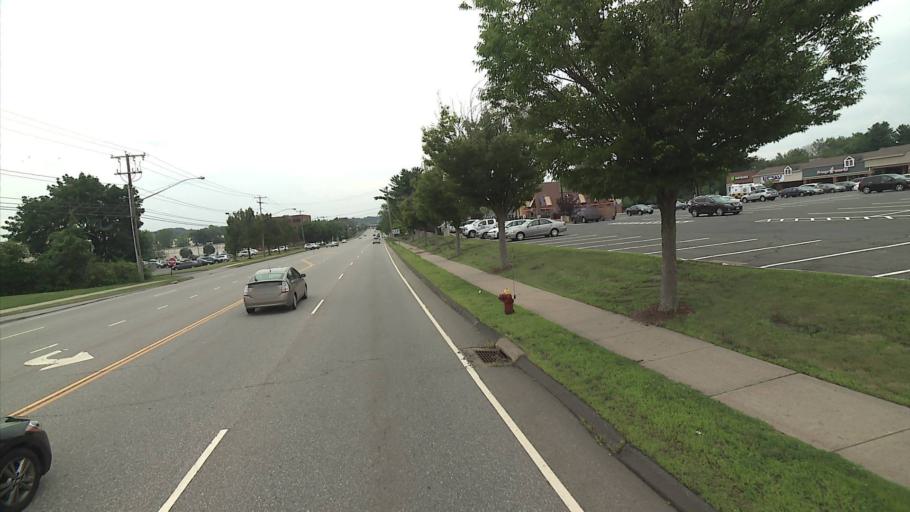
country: US
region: Connecticut
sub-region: Hartford County
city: Wethersfield
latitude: 41.6925
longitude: -72.6564
